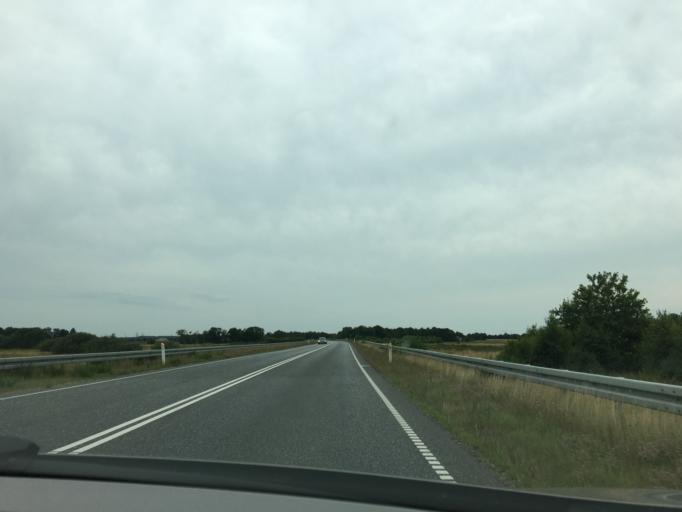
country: DK
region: Central Jutland
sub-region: Herning Kommune
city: Sunds
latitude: 56.2177
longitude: 9.0035
